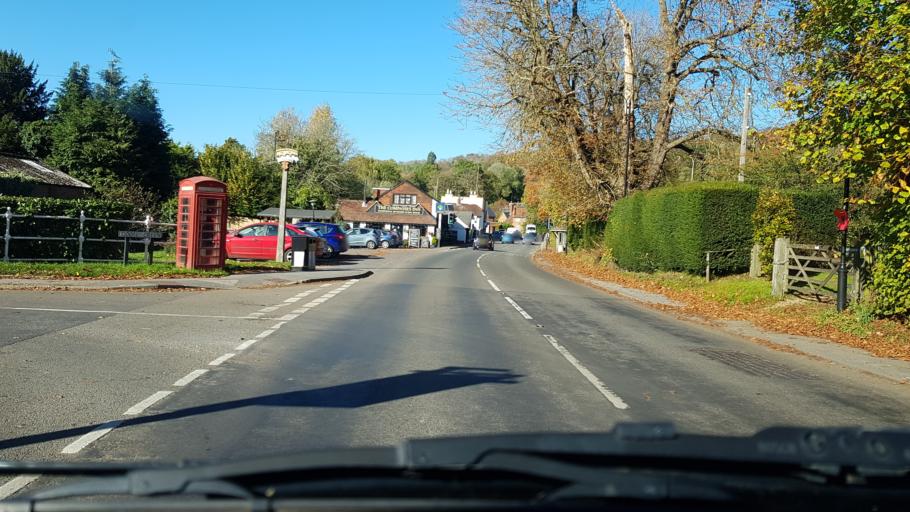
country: GB
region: England
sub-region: Surrey
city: East Horsley
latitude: 51.2195
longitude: -0.4471
